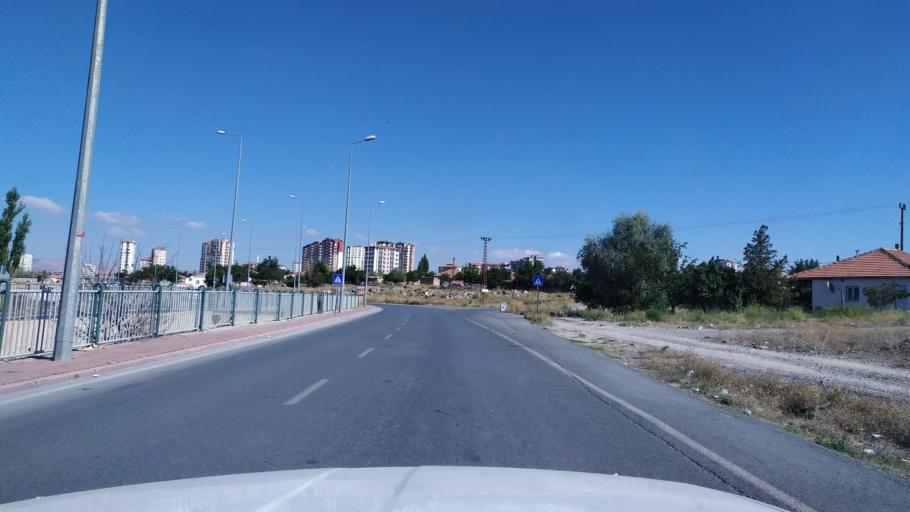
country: TR
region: Kayseri
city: Talas
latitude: 38.7321
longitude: 35.5492
